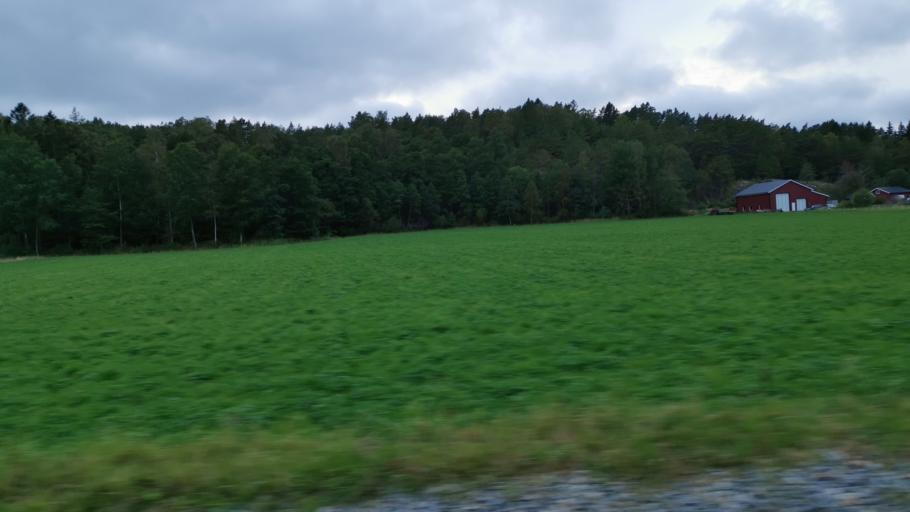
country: SE
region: Vaestra Goetaland
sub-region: Tanums Kommun
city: Tanumshede
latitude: 58.6335
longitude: 11.3455
